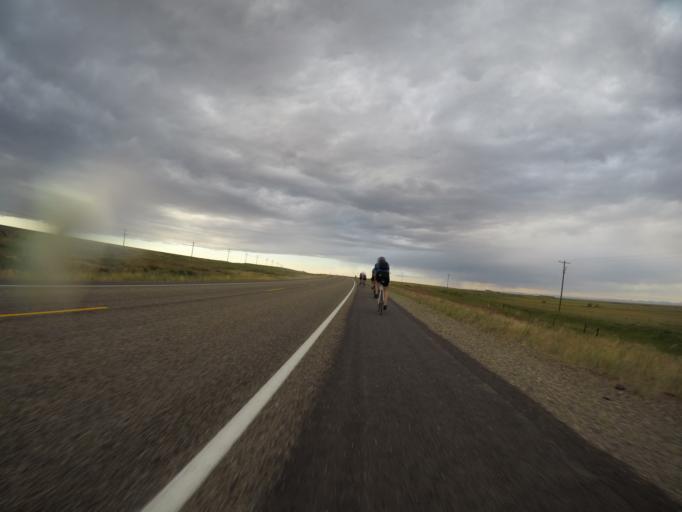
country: US
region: Wyoming
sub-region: Albany County
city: Laramie
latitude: 41.8066
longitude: -105.9856
